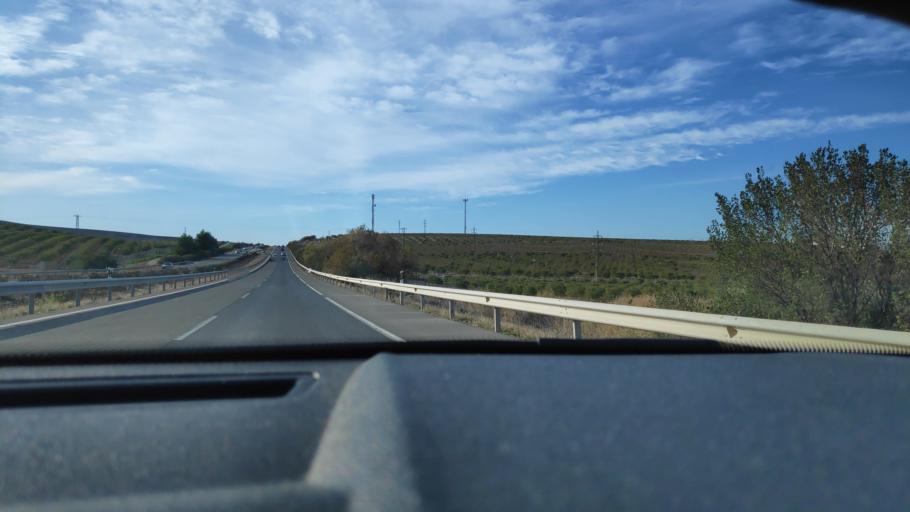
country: ES
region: Andalusia
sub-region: Province of Cordoba
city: Villafranca de Cordoba
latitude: 37.9048
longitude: -4.6222
